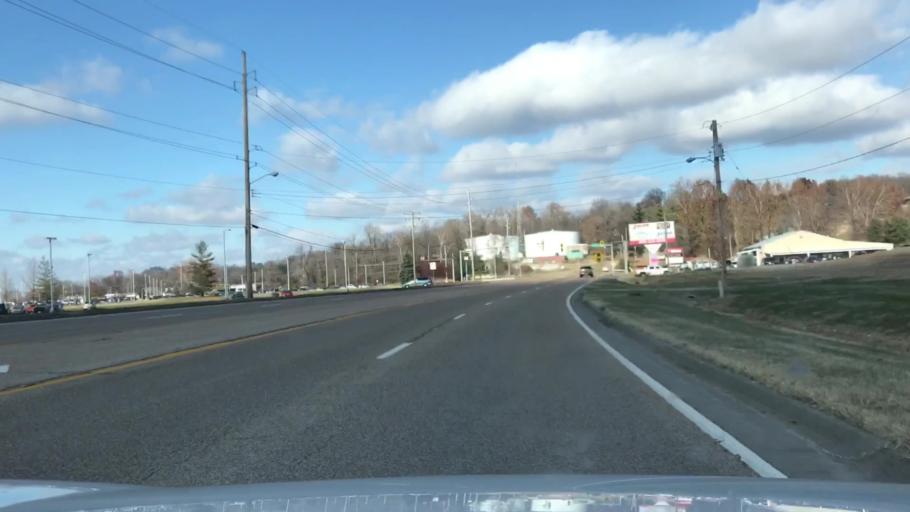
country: US
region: Illinois
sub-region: Saint Clair County
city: Caseyville
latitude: 38.5923
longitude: -90.0457
